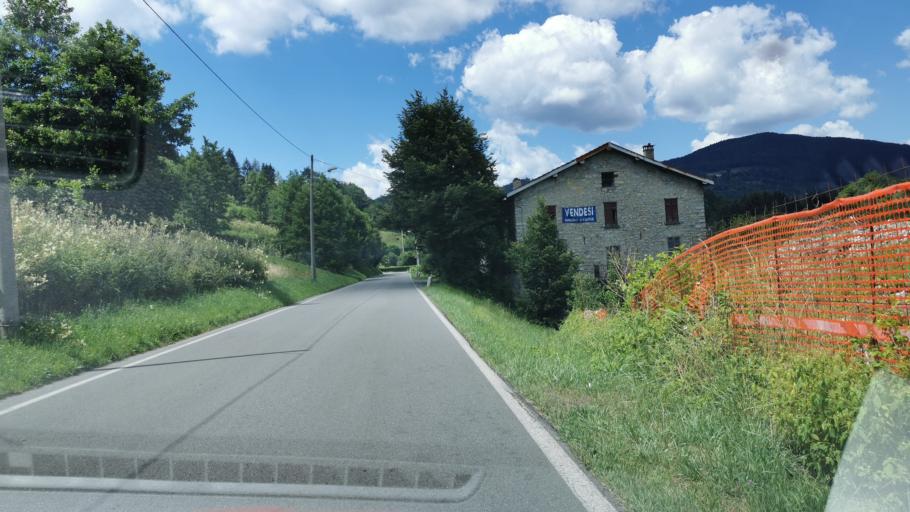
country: IT
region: Lombardy
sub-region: Provincia di Como
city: San Fedele Superiore
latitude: 45.9724
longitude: 9.0684
